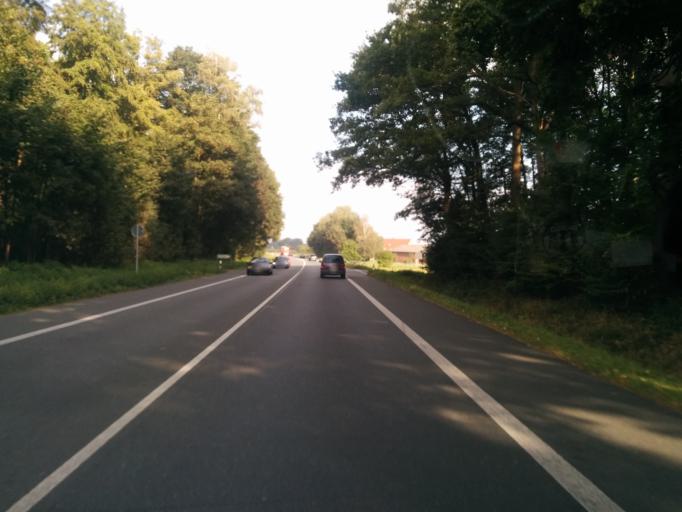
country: DE
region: North Rhine-Westphalia
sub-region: Regierungsbezirk Munster
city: Dulmen
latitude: 51.8763
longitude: 7.2200
